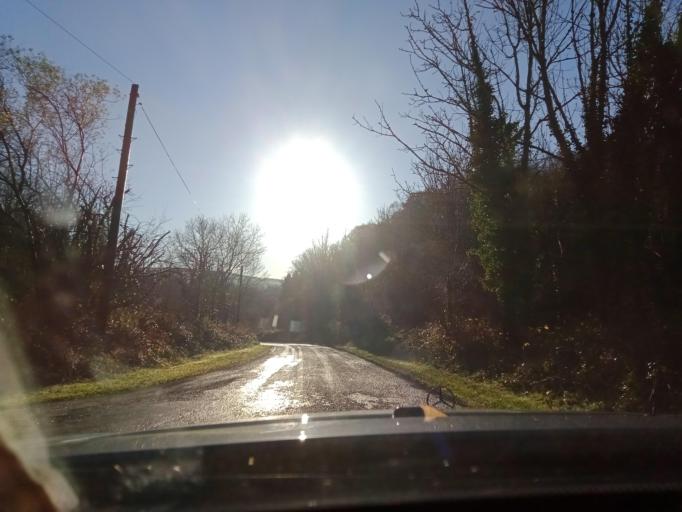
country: IE
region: Munster
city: Carrick-on-Suir
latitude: 52.4229
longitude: -7.3842
